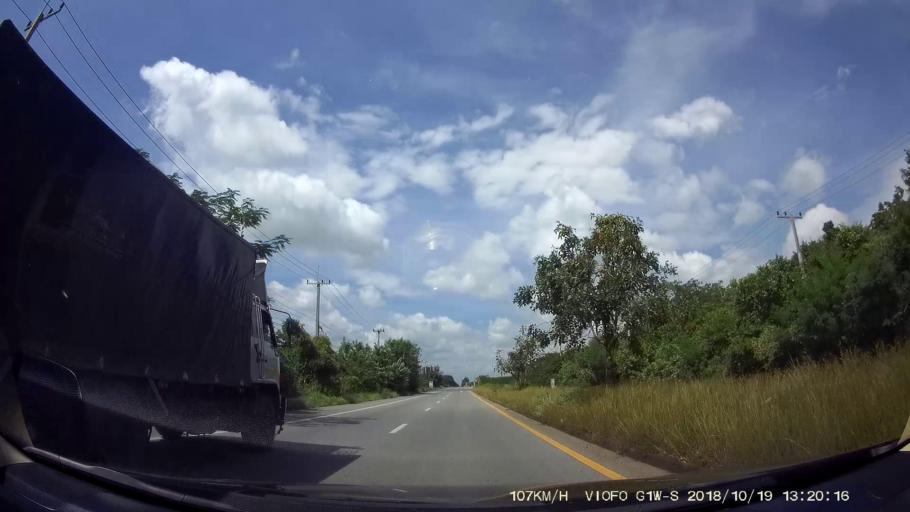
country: TH
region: Chaiyaphum
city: Chatturat
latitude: 15.4431
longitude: 101.8290
